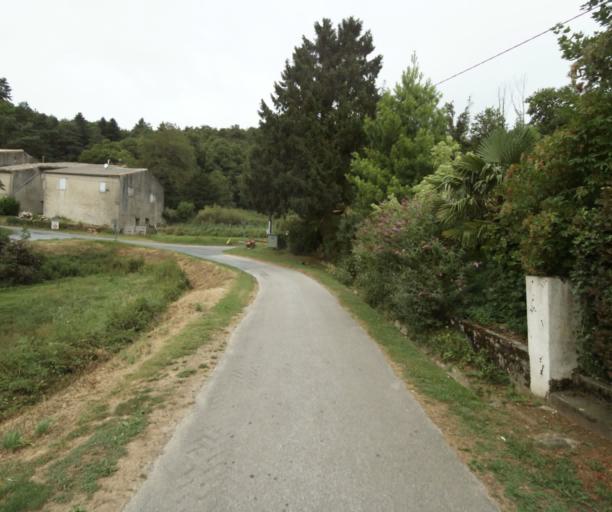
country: FR
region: Midi-Pyrenees
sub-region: Departement du Tarn
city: Soreze
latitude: 43.4135
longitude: 2.0836
